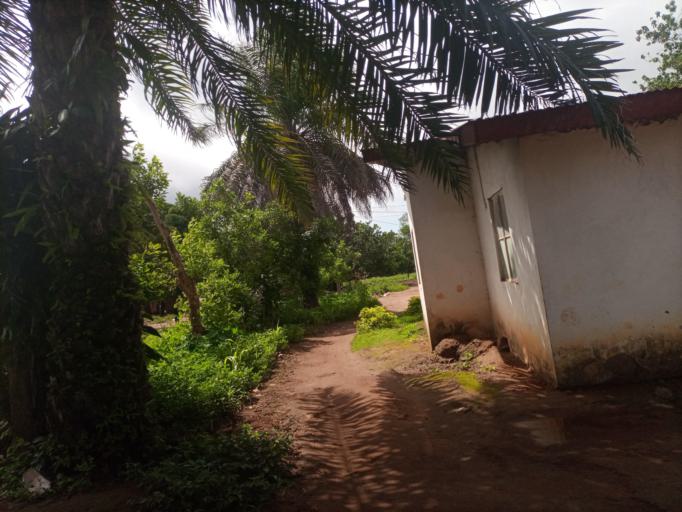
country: SL
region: Northern Province
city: Tintafor
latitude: 8.6366
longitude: -13.2125
